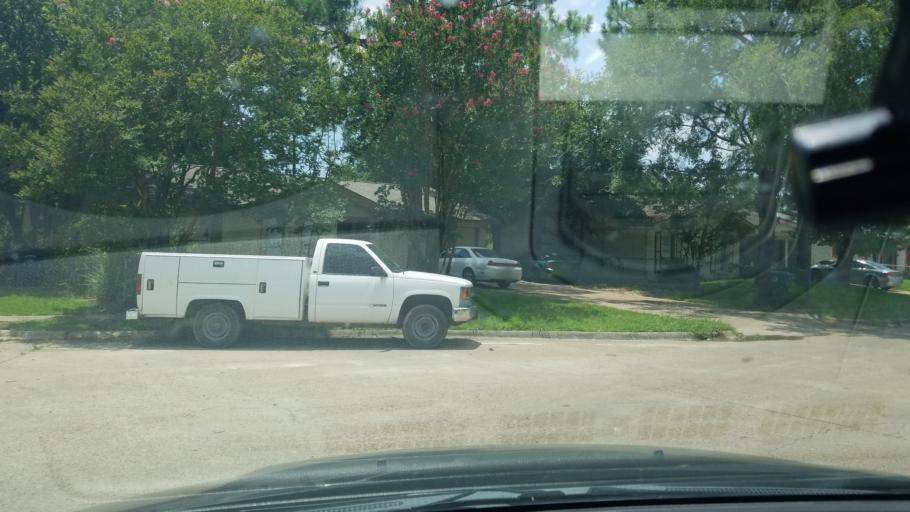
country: US
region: Texas
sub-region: Dallas County
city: Balch Springs
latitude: 32.7132
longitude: -96.6502
